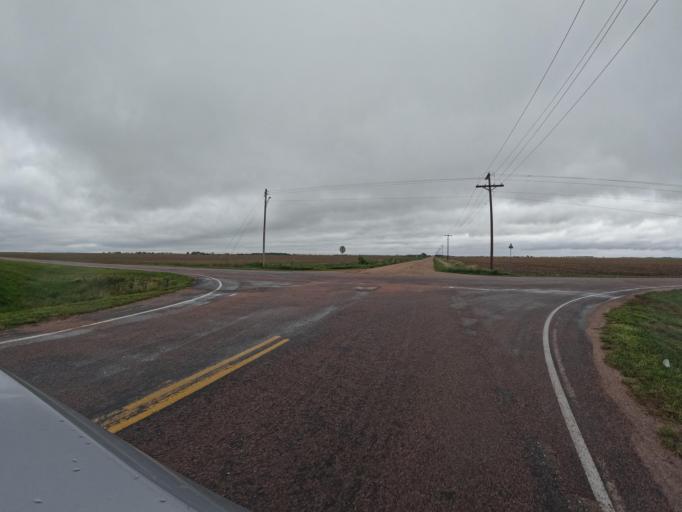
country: US
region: Nebraska
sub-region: Clay County
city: Harvard
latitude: 40.6259
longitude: -98.0900
